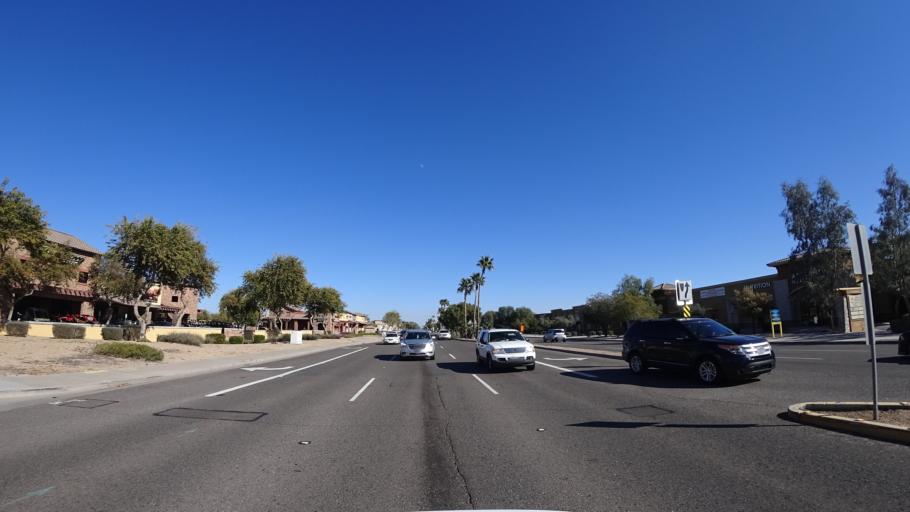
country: US
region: Arizona
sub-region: Maricopa County
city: Sun City West
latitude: 33.6388
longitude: -112.3919
